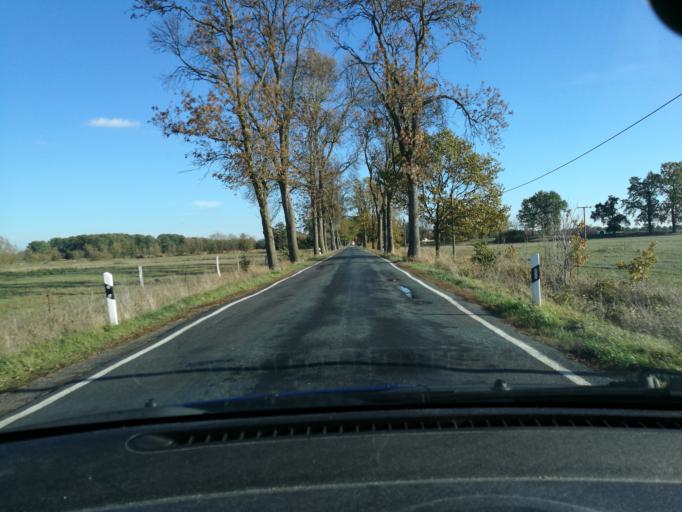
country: DE
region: Brandenburg
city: Lenzen
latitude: 53.1098
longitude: 11.4134
